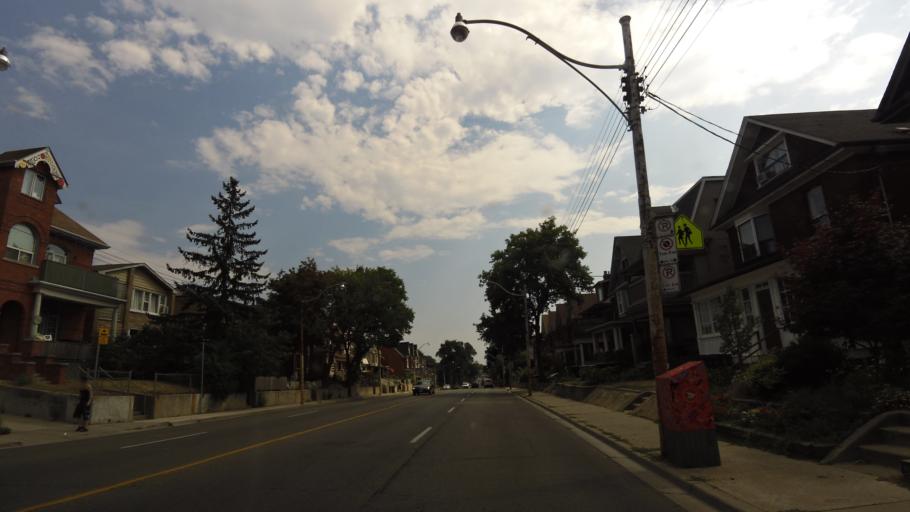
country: CA
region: Ontario
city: Toronto
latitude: 43.6614
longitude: -79.4629
